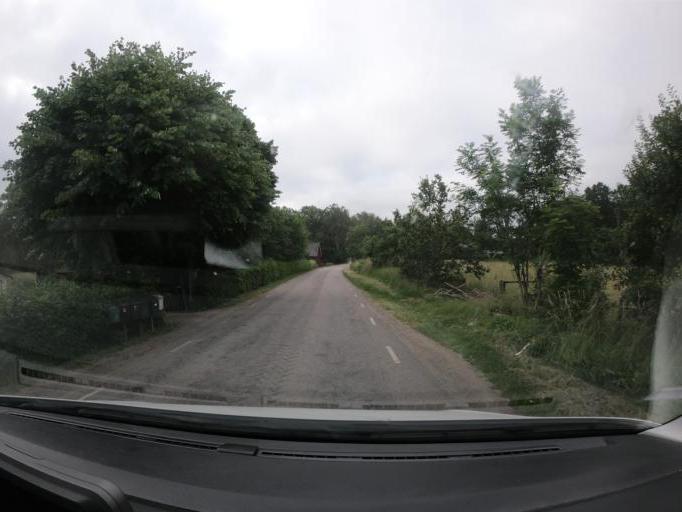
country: SE
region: Skane
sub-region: Klippans Kommun
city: Ljungbyhed
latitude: 56.0512
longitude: 13.2547
